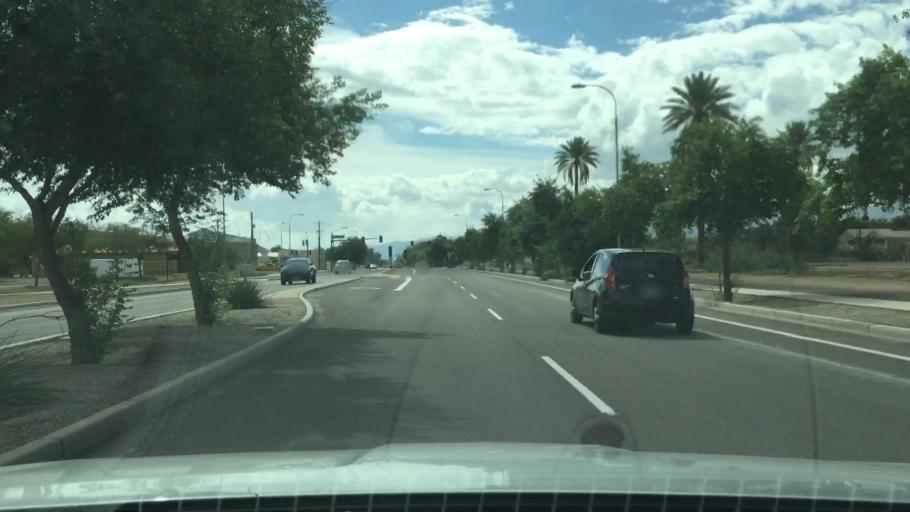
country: US
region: Arizona
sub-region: Maricopa County
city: Laveen
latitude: 33.3647
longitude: -112.1692
